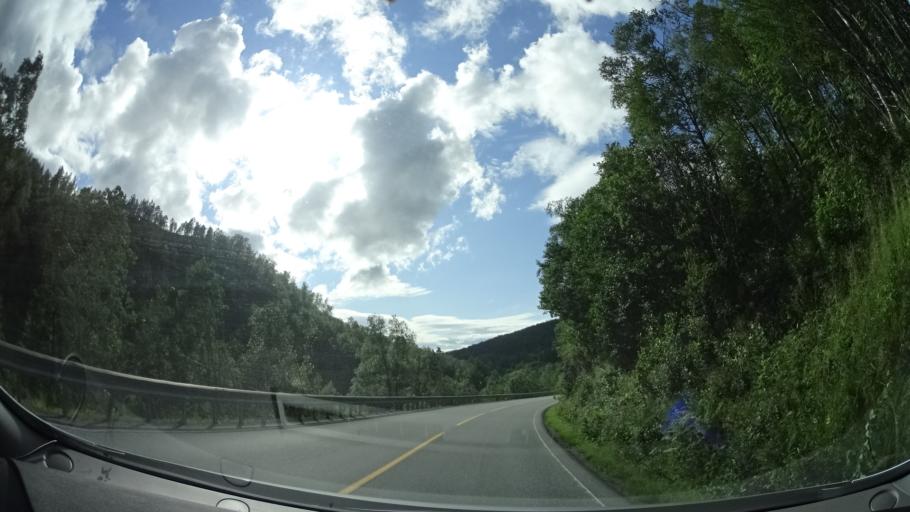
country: NO
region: Sor-Trondelag
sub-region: Hemne
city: Kyrksaeterora
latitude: 63.2148
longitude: 9.1241
